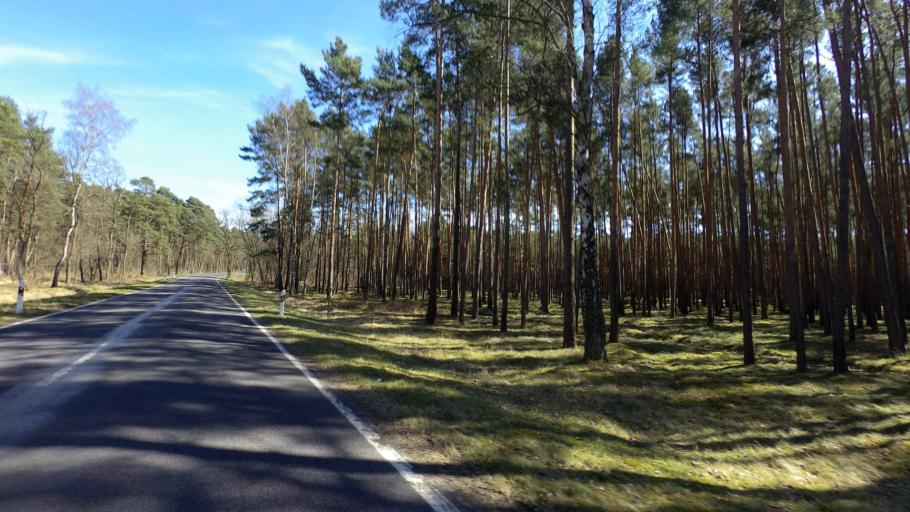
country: DE
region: Brandenburg
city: Munchehofe
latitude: 52.1600
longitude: 13.8970
